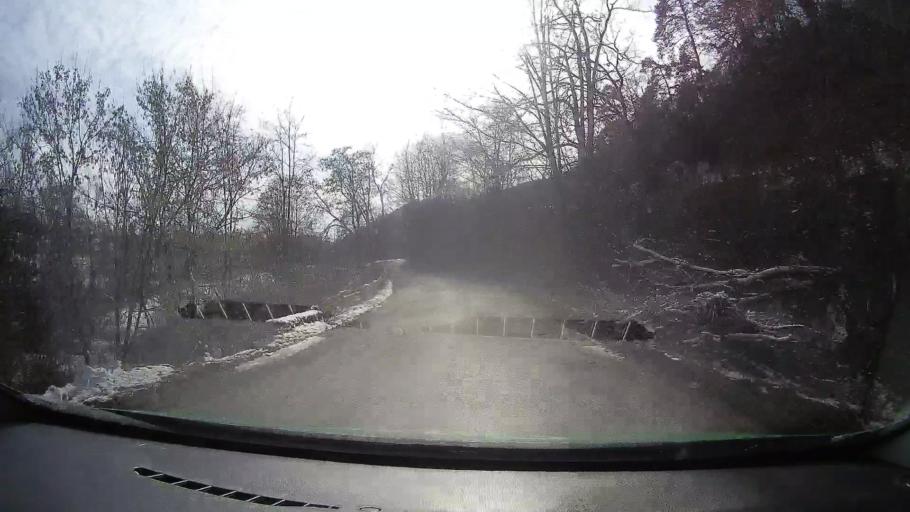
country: RO
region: Mures
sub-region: Municipiul Sighisoara
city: Sighisoara
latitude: 46.1993
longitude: 24.7683
